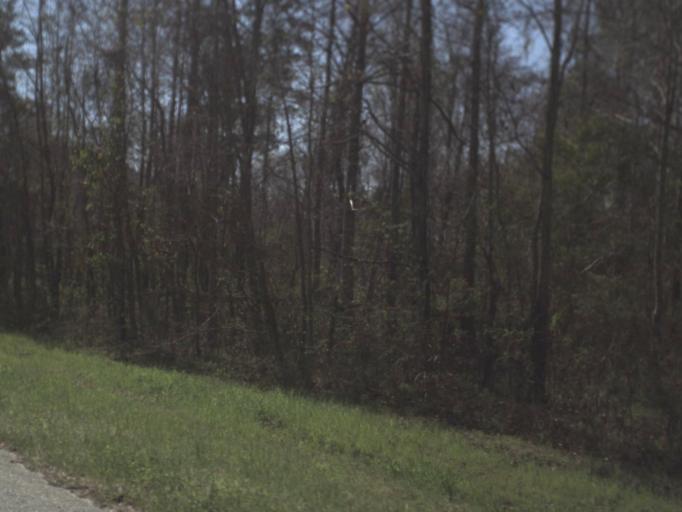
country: US
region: Florida
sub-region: Jefferson County
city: Monticello
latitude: 30.3765
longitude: -84.0030
